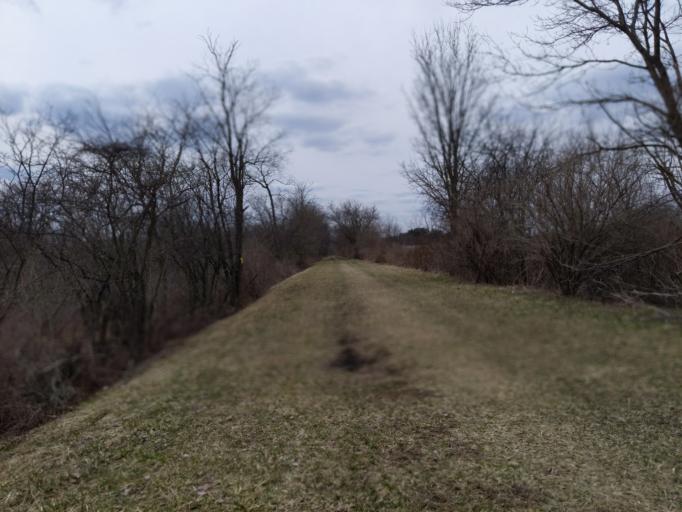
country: US
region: New York
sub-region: Tompkins County
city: Dryden
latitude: 42.4968
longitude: -76.3197
